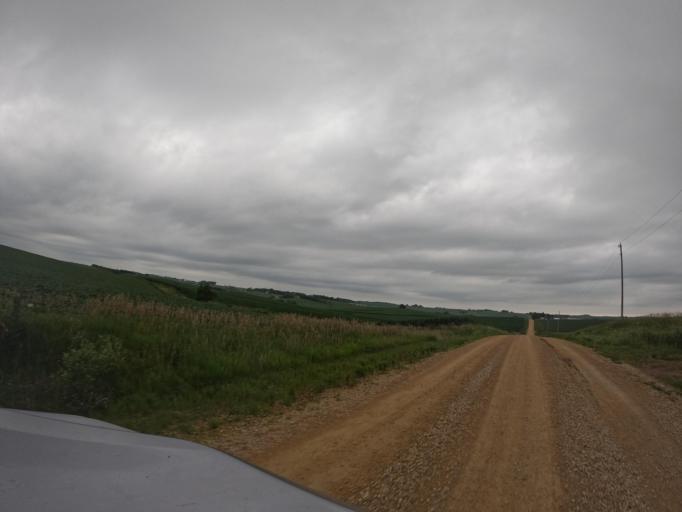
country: US
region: Iowa
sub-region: Jackson County
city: Maquoketa
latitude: 41.9450
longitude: -90.6454
